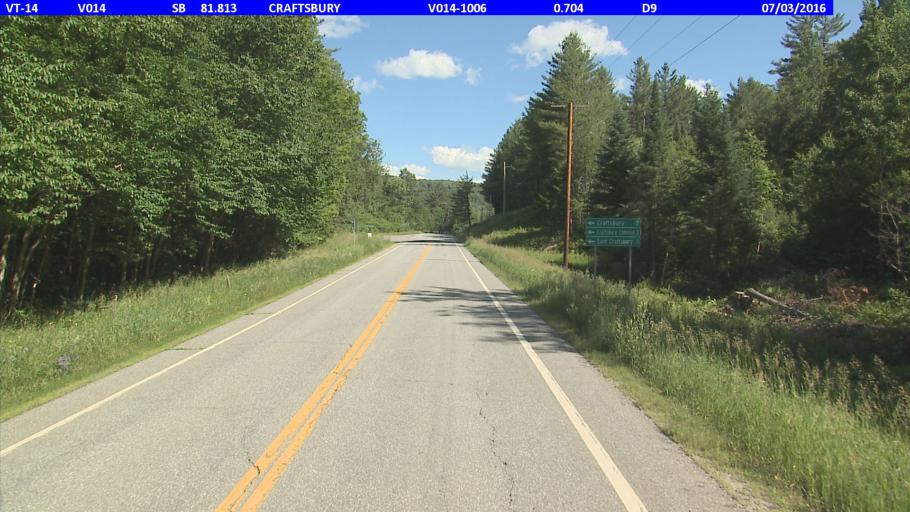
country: US
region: Vermont
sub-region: Caledonia County
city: Hardwick
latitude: 44.6156
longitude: -72.3632
